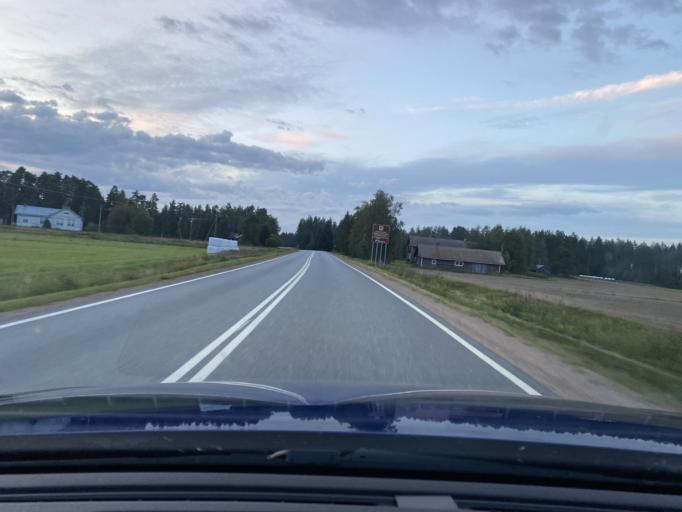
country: FI
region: Satakunta
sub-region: Pohjois-Satakunta
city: Honkajoki
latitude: 62.1465
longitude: 22.2636
